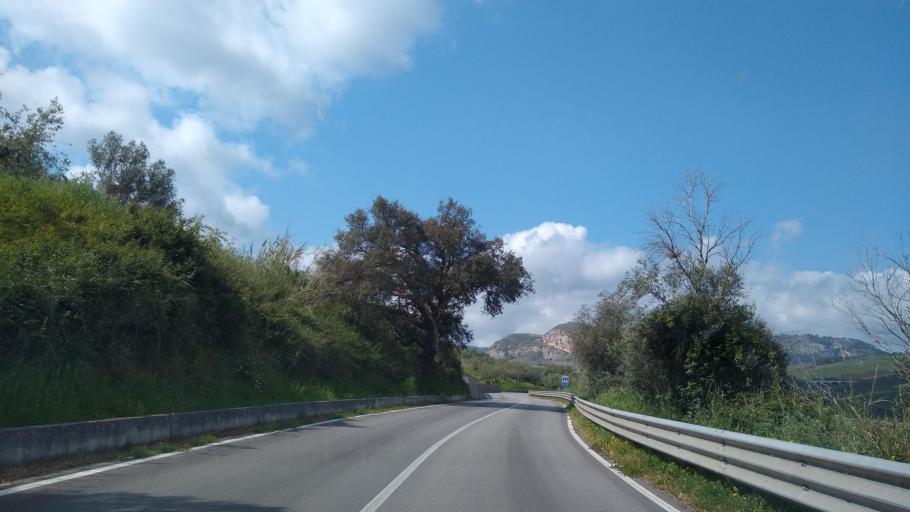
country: IT
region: Sicily
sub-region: Trapani
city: Calatafimi
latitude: 37.9560
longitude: 12.8677
